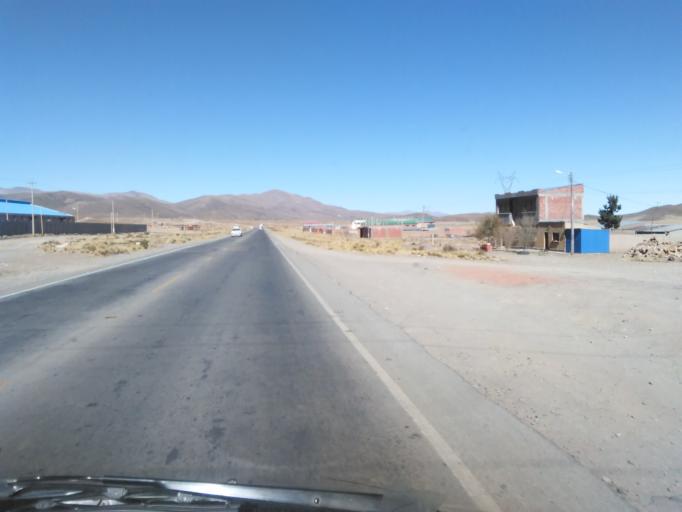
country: BO
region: Oruro
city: Oruro
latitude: -18.0220
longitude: -67.0280
